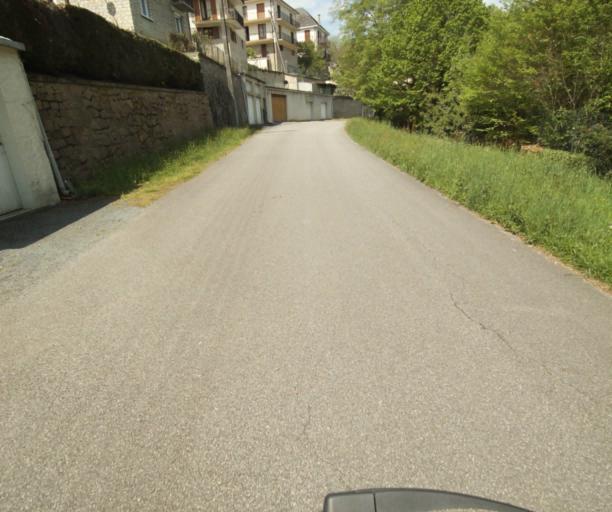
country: FR
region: Limousin
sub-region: Departement de la Correze
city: Tulle
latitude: 45.2717
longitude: 1.7654
